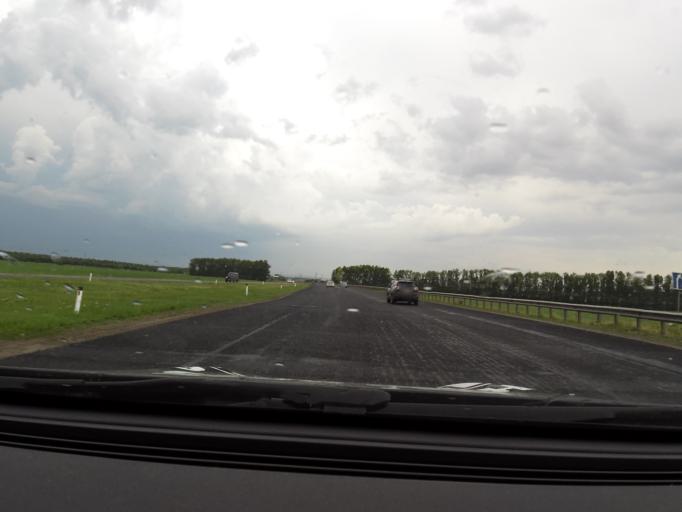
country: RU
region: Bashkortostan
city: Asanovo
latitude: 54.9545
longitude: 55.5852
